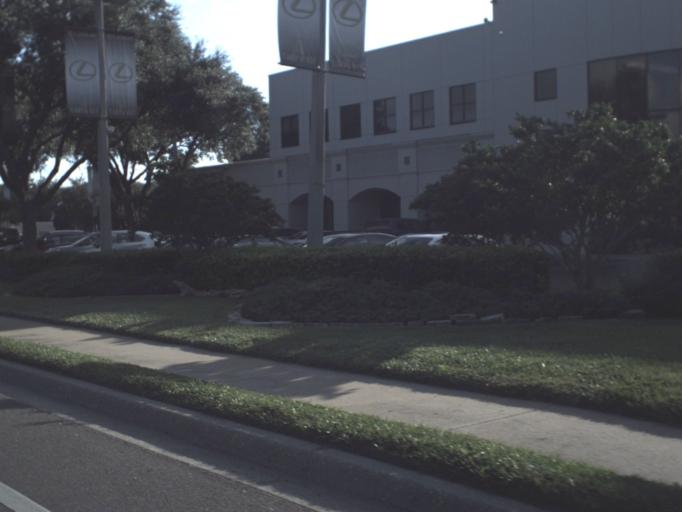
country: US
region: Florida
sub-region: Hillsborough County
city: Egypt Lake-Leto
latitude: 28.0017
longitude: -82.5053
